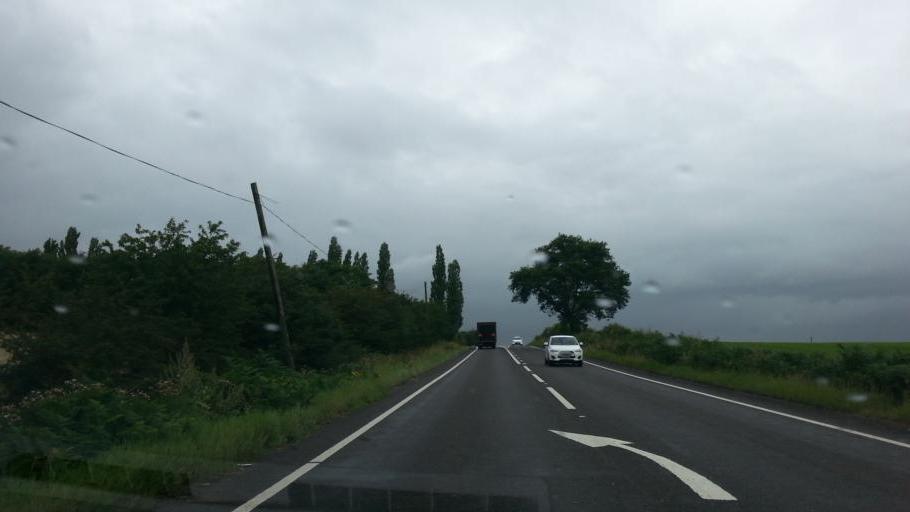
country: GB
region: England
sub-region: Nottinghamshire
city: Bilsthorpe
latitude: 53.1588
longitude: -1.0465
